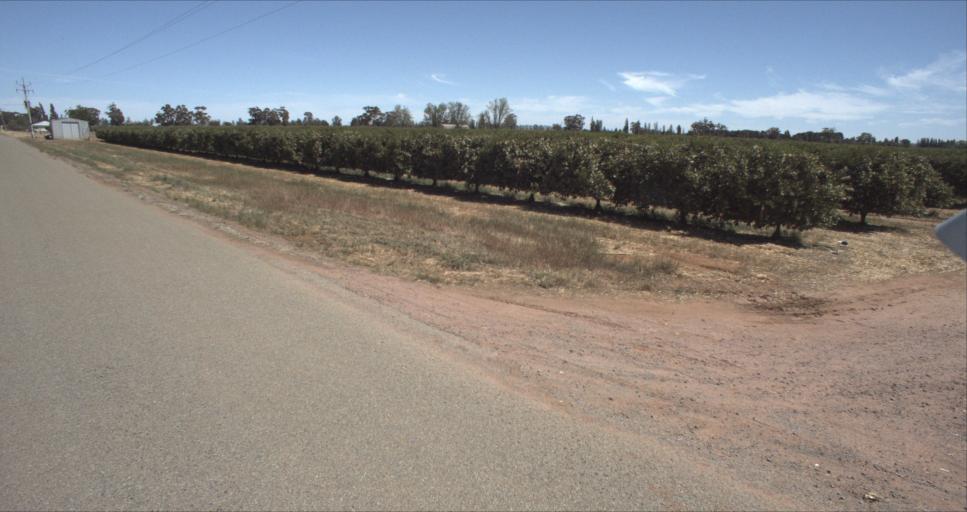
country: AU
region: New South Wales
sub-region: Leeton
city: Leeton
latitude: -34.5390
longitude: 146.3521
